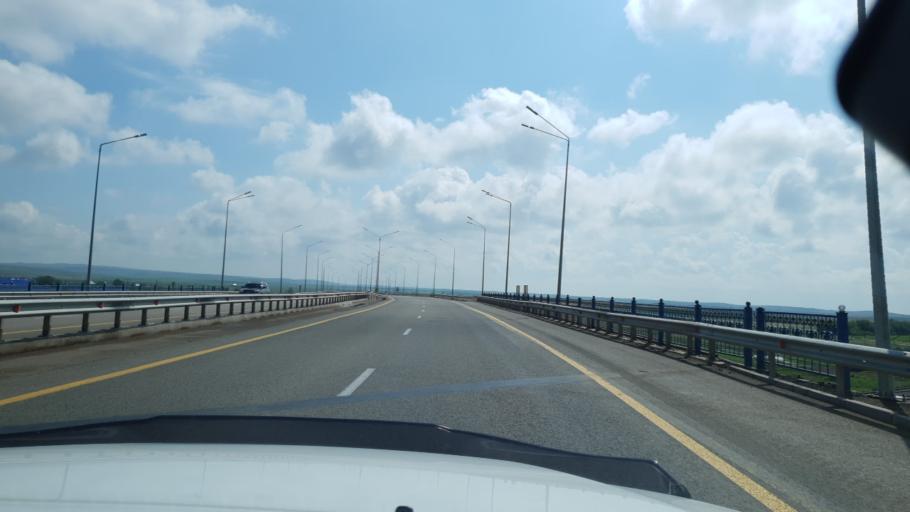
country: KZ
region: Qaraghandy
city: Osakarovka
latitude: 50.8111
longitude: 72.1771
